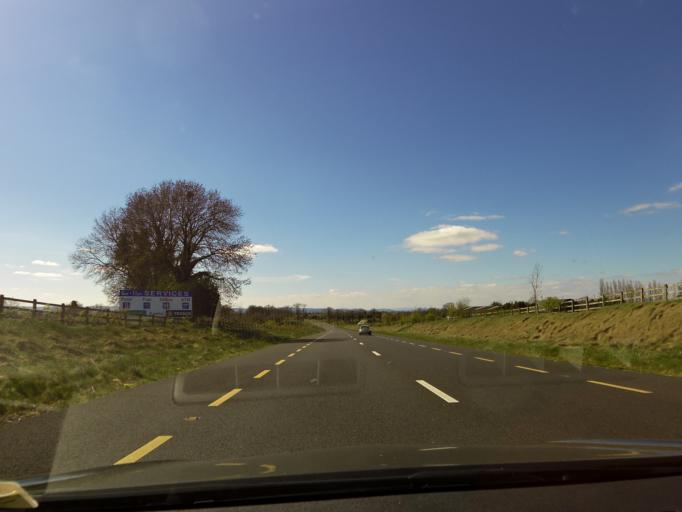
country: IE
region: Leinster
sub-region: Kildare
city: Moone
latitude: 52.9986
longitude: -6.8571
